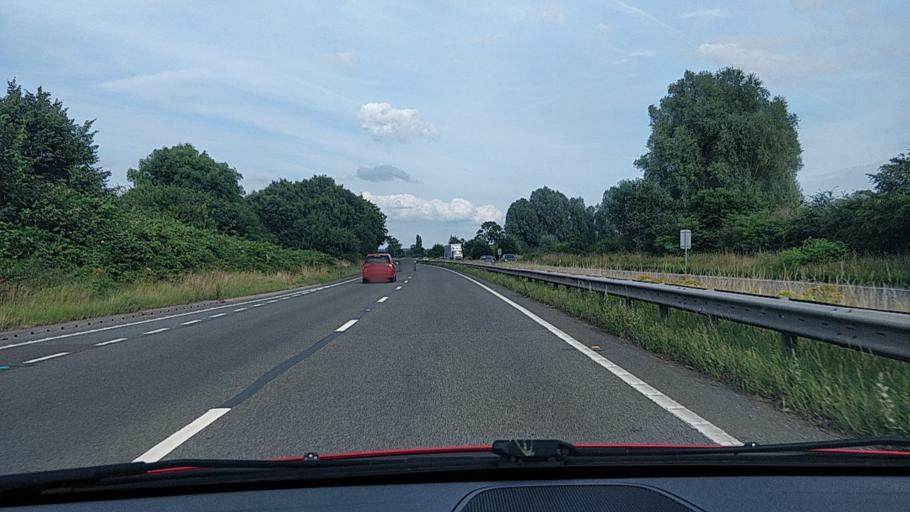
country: GB
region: Wales
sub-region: County of Flintshire
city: Hawarden
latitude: 53.1601
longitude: -2.9998
